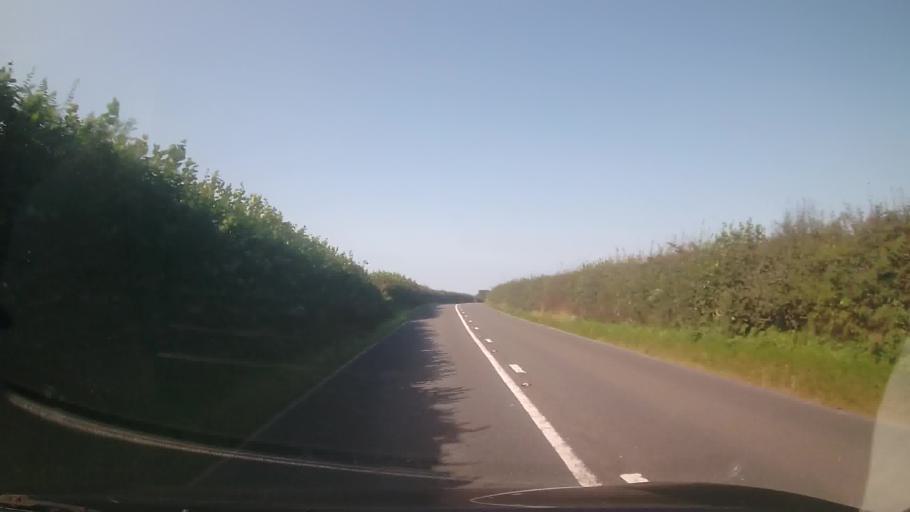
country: GB
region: Wales
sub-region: Sir Powys
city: Builth Wells
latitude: 52.1507
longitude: -3.4440
